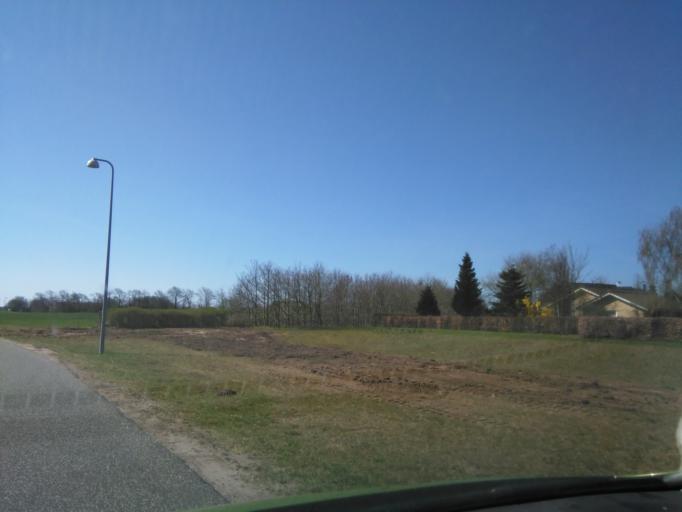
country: DK
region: South Denmark
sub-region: Billund Kommune
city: Billund
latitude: 55.7139
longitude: 9.1149
